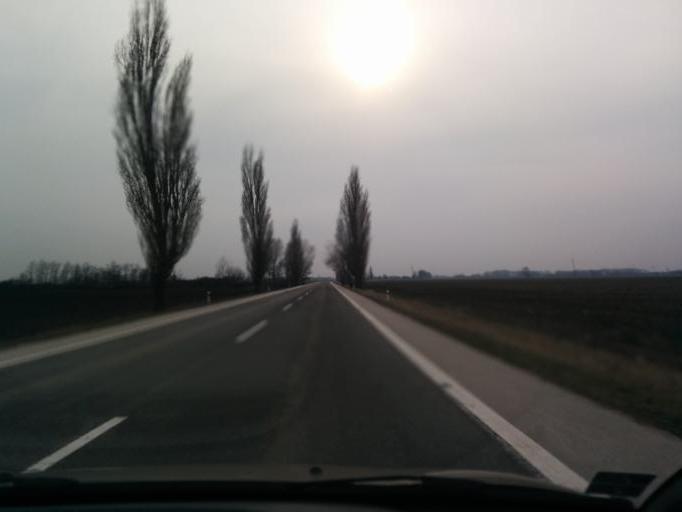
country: SK
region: Trnavsky
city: Sladkovicovo
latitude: 48.2257
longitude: 17.6743
